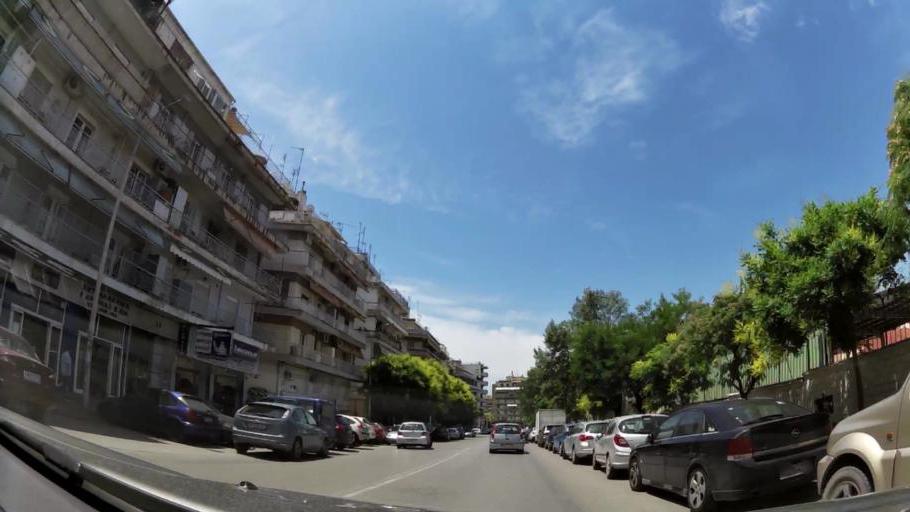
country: GR
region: Central Macedonia
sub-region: Nomos Thessalonikis
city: Agios Pavlos
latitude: 40.6225
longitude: 22.9588
